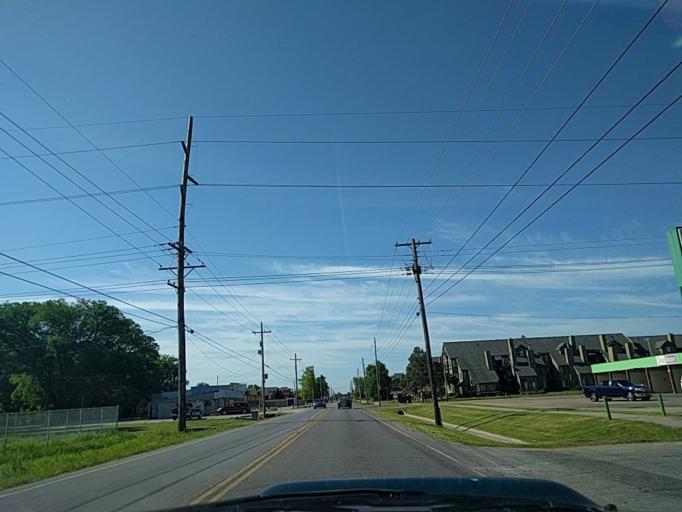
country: US
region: Oklahoma
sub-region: Tulsa County
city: Jenks
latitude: 36.0683
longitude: -95.9758
